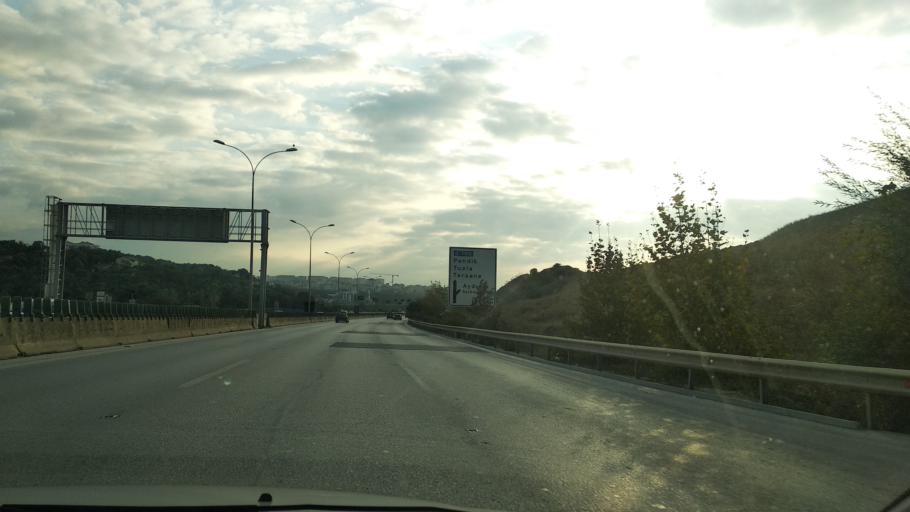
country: TR
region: Istanbul
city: Icmeler
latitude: 40.8860
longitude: 29.3228
